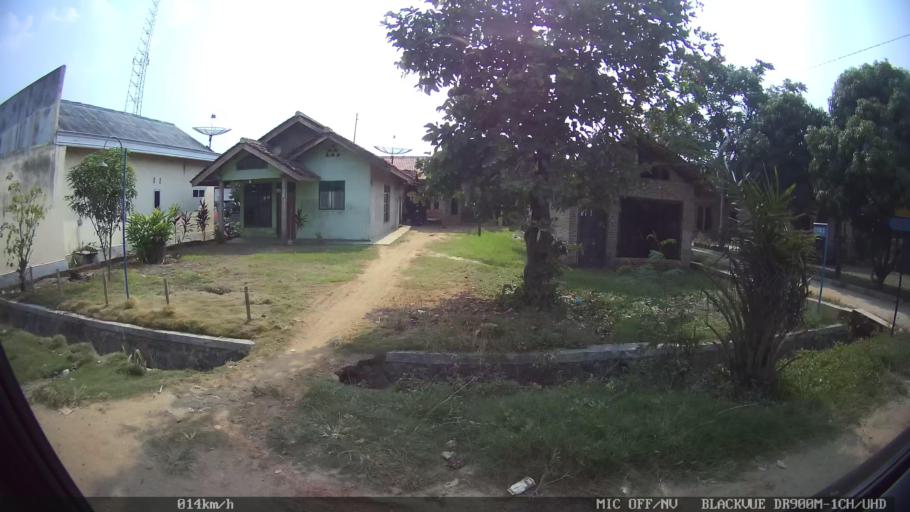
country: ID
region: Lampung
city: Kedondong
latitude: -5.4096
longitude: 104.9930
